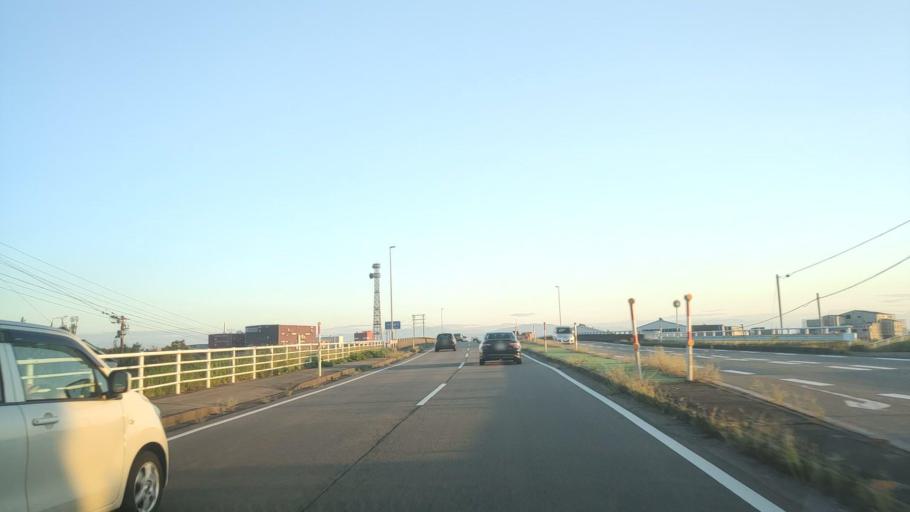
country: JP
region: Toyama
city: Takaoka
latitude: 36.7762
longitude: 136.9999
